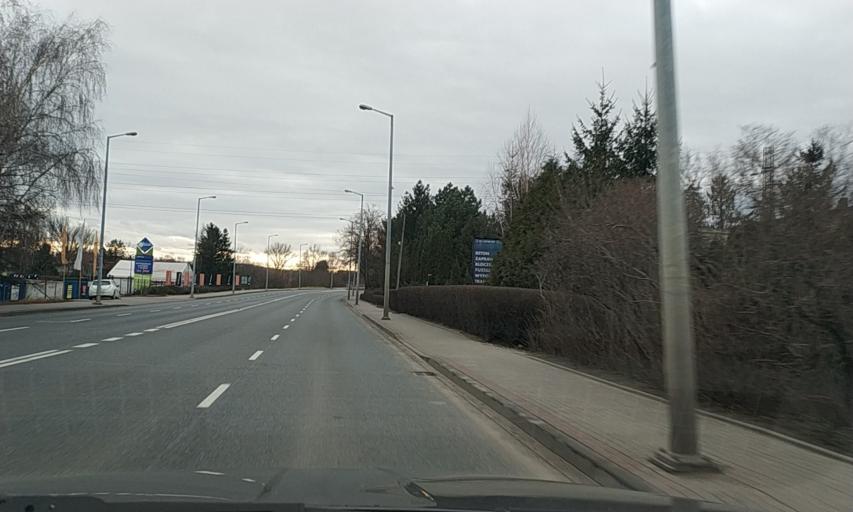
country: PL
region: Lesser Poland Voivodeship
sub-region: Powiat tarnowski
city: Koszyce Wielkie
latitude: 49.9983
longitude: 20.9533
